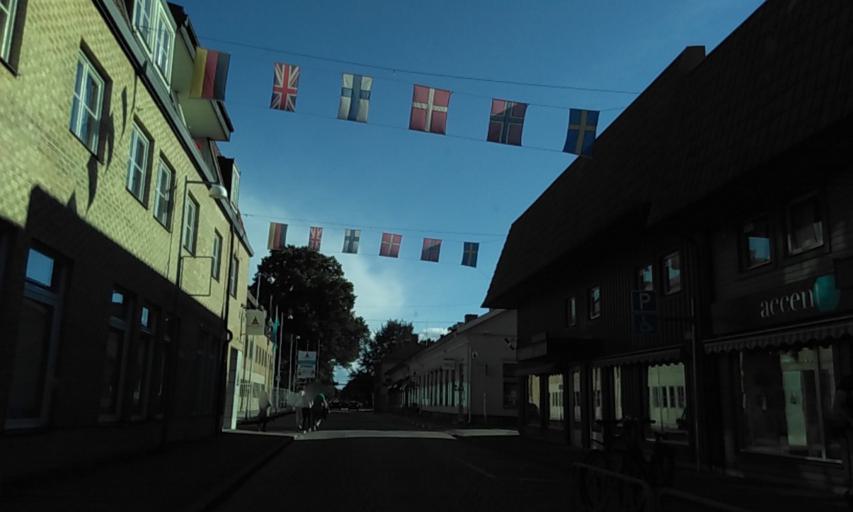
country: SE
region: Vaestra Goetaland
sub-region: Lidkopings Kommun
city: Lidkoping
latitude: 58.5027
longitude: 13.1554
